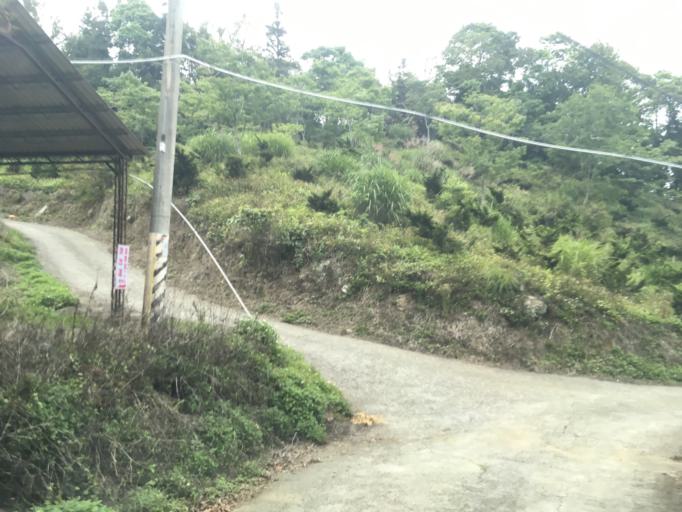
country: TW
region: Taiwan
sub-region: Nantou
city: Puli
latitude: 23.9655
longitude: 120.8381
